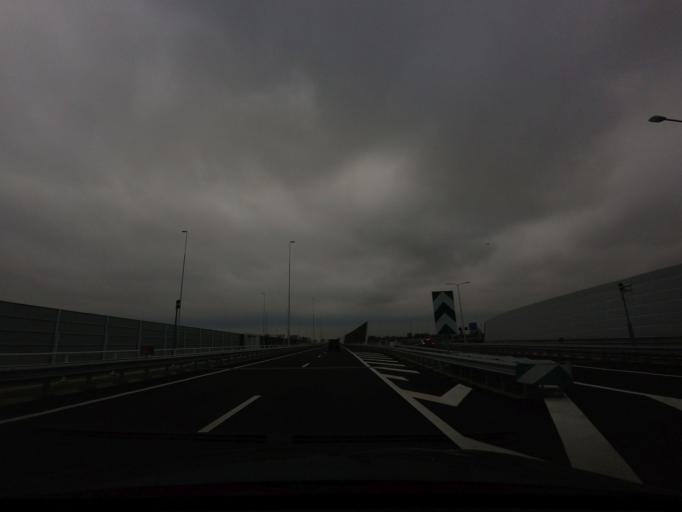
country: NL
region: South Holland
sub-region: Gemeente Schiedam
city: Schiedam
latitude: 51.9280
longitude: 4.3648
